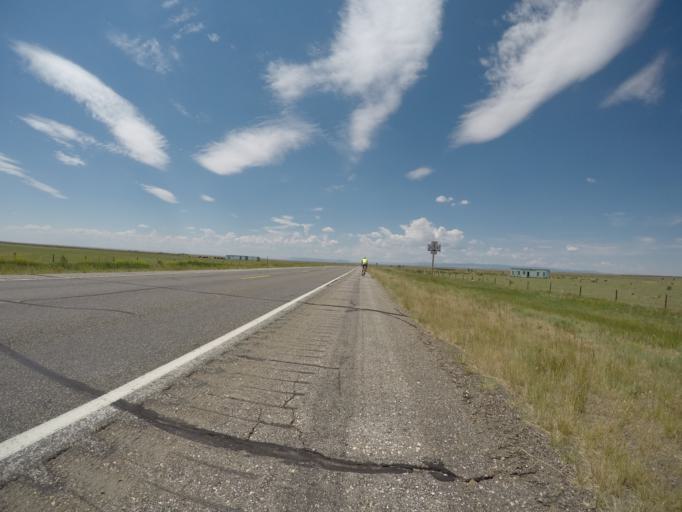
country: US
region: Wyoming
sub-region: Albany County
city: Laramie
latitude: 41.5586
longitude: -105.6724
